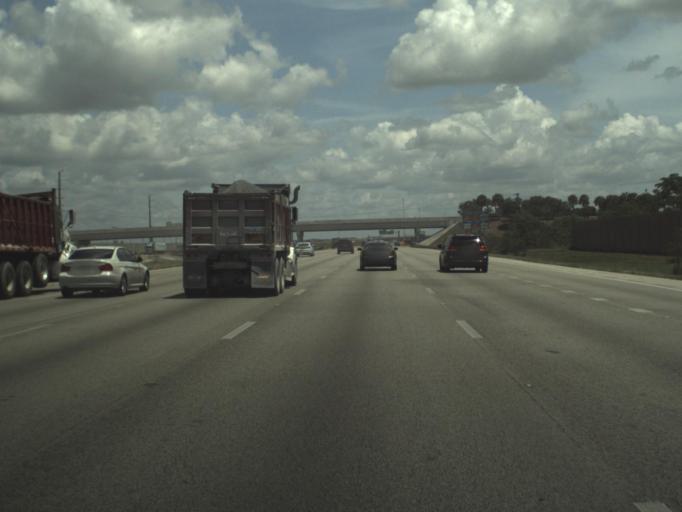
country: US
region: Florida
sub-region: Miami-Dade County
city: Palm Springs North
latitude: 25.9653
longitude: -80.3517
